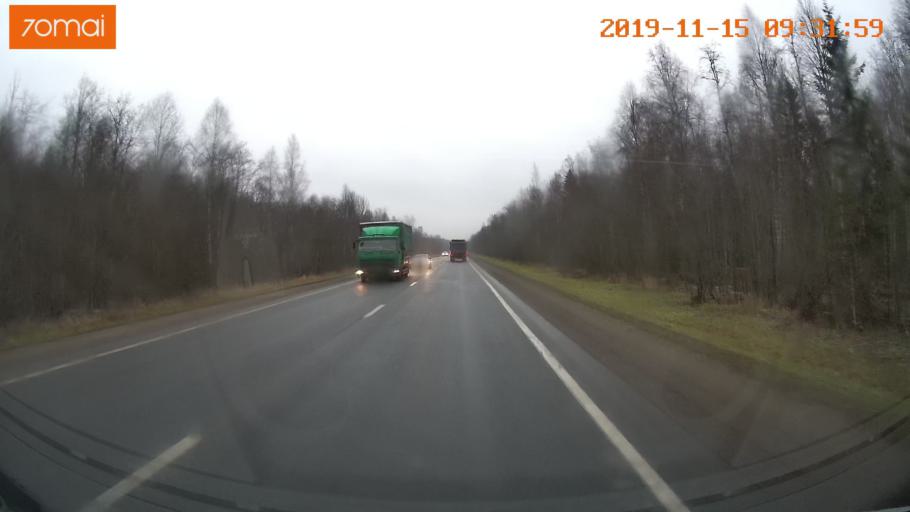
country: RU
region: Vologda
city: Sheksna
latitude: 59.2733
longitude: 38.3239
